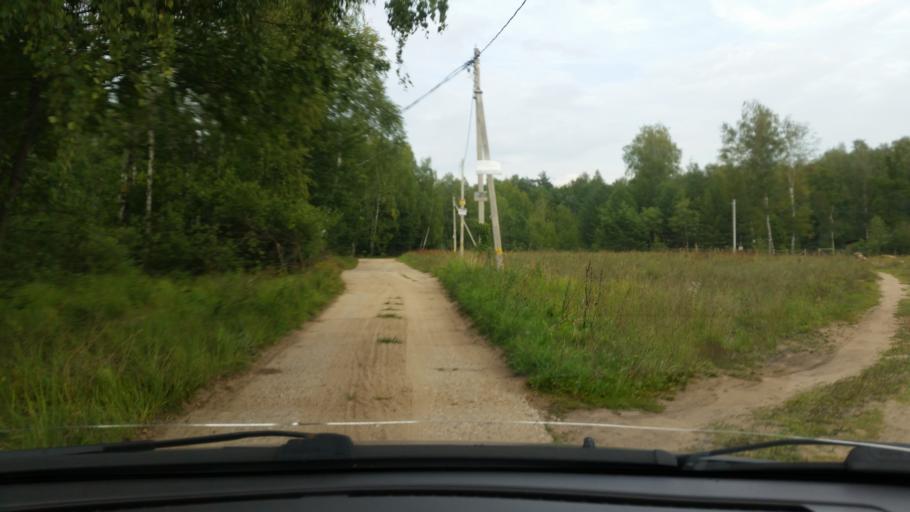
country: RU
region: Moskovskaya
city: Bol'shoye Gryzlovo
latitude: 54.8515
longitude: 37.7107
